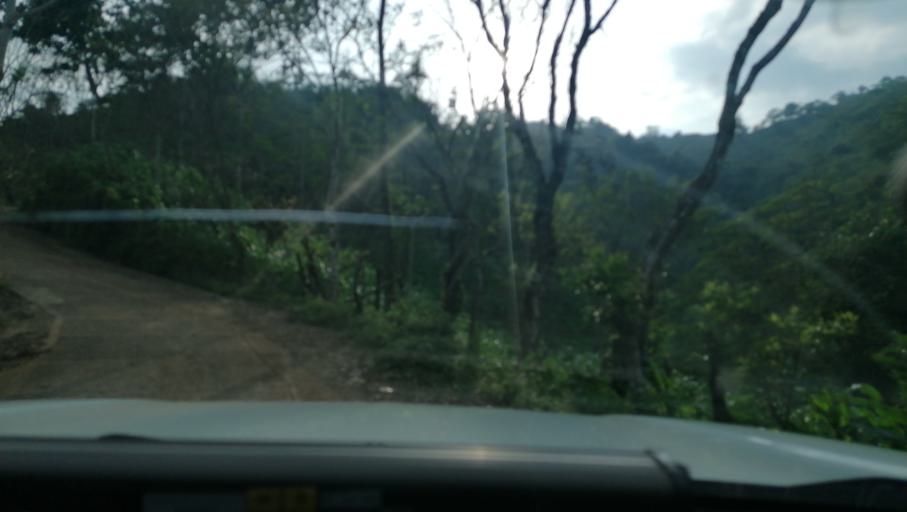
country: MX
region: Chiapas
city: Ixtacomitan
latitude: 17.3322
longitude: -93.1052
